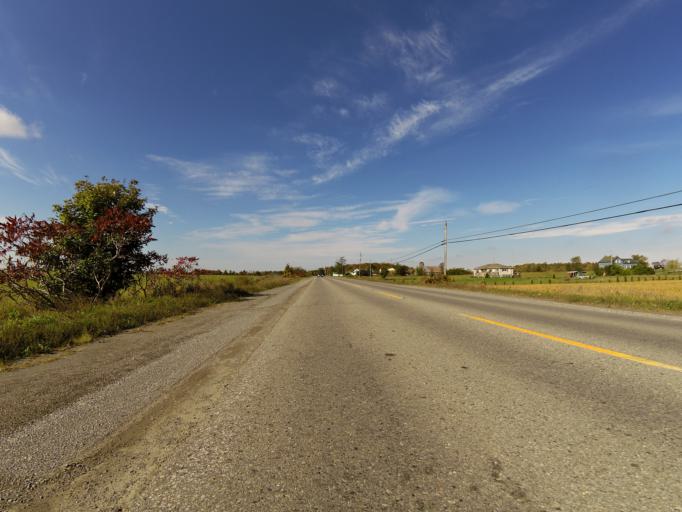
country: CA
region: Ontario
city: Prince Edward
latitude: 44.0105
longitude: -77.2681
